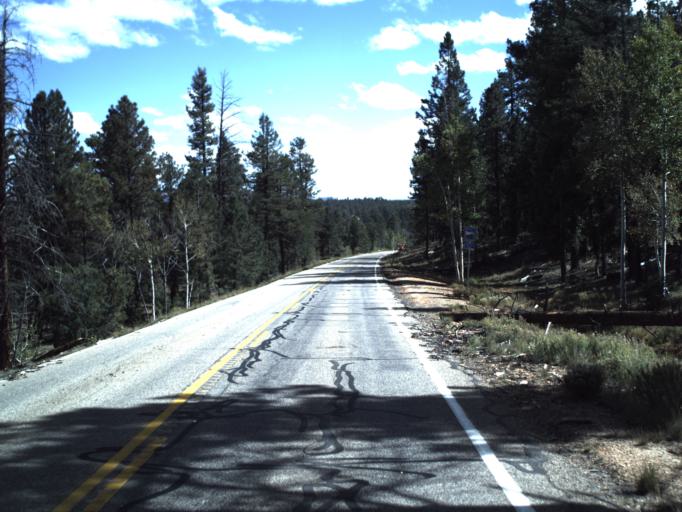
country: US
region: Utah
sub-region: Garfield County
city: Panguitch
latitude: 37.5128
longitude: -112.6343
